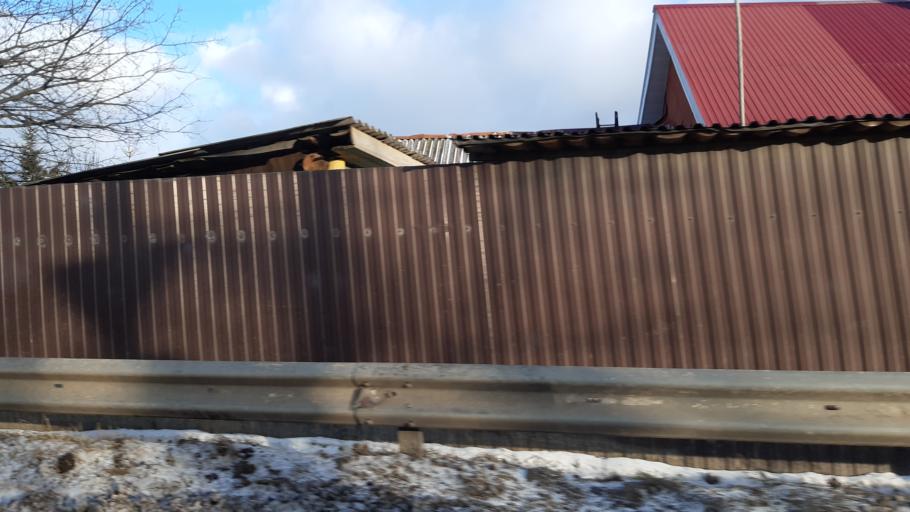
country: RU
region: Moskovskaya
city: Noginsk-9
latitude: 56.0522
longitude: 38.5508
